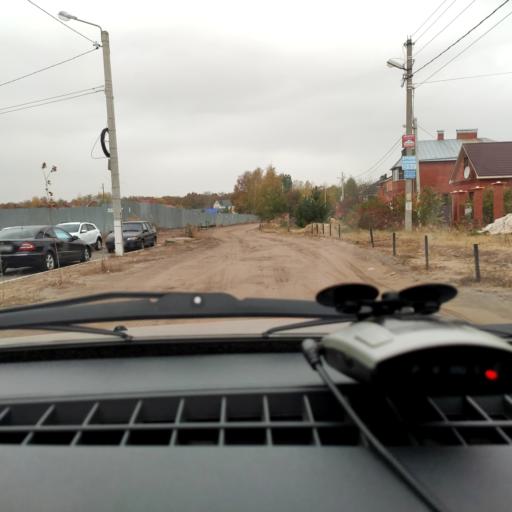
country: RU
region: Voronezj
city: Podgornoye
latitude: 51.7611
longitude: 39.1805
